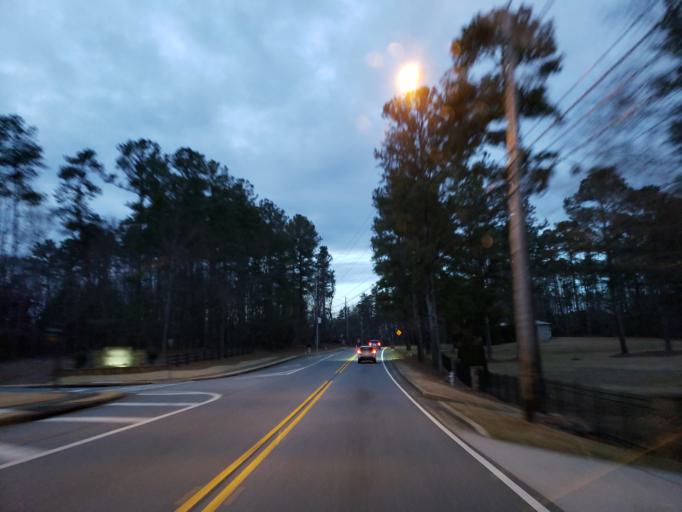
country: US
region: Georgia
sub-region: Cobb County
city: Kennesaw
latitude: 33.9781
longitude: -84.6695
